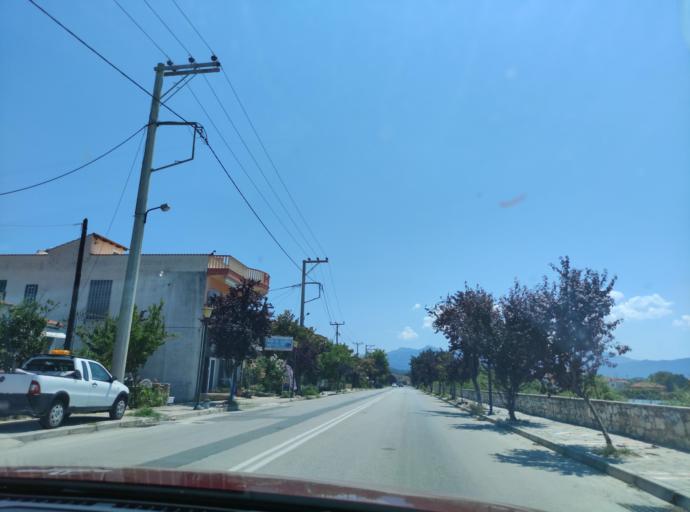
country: GR
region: East Macedonia and Thrace
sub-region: Nomos Kavalas
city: Keramoti
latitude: 40.8632
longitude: 24.7058
